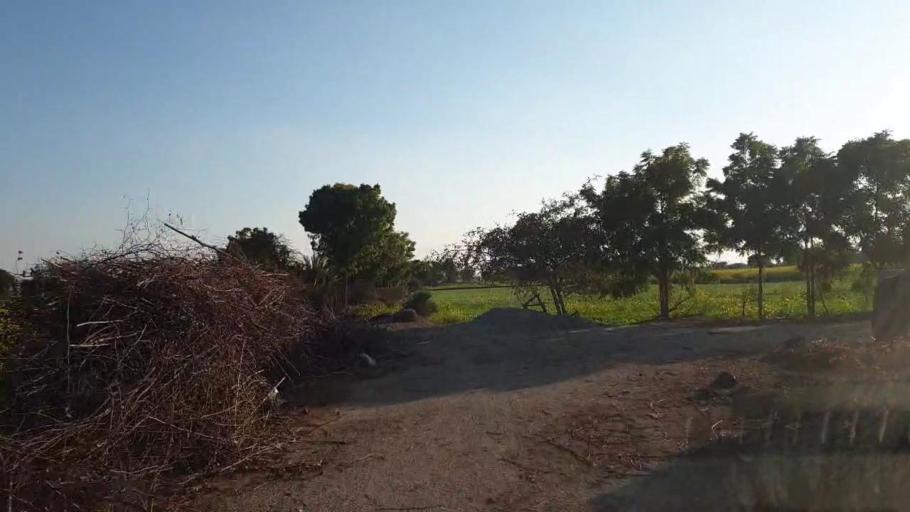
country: PK
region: Sindh
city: Shahpur Chakar
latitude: 26.1475
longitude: 68.5308
